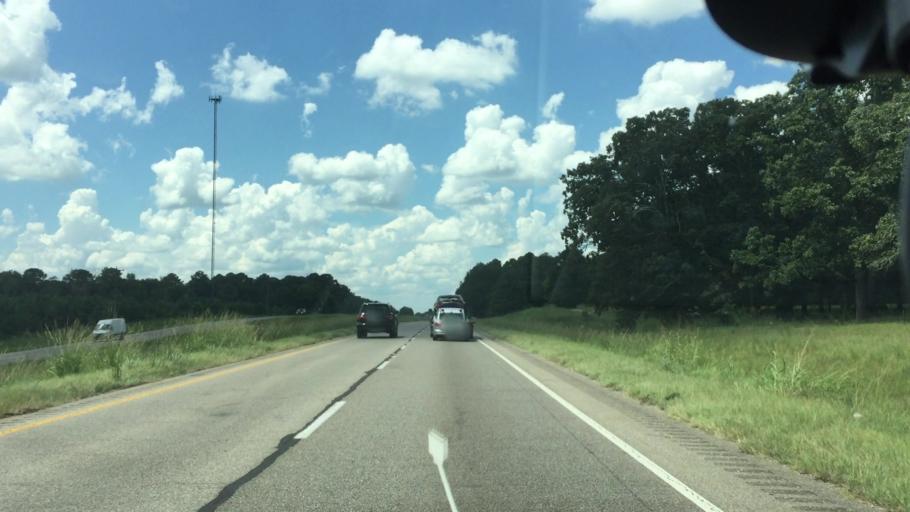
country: US
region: Alabama
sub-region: Montgomery County
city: Pike Road
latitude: 32.1266
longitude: -86.0790
